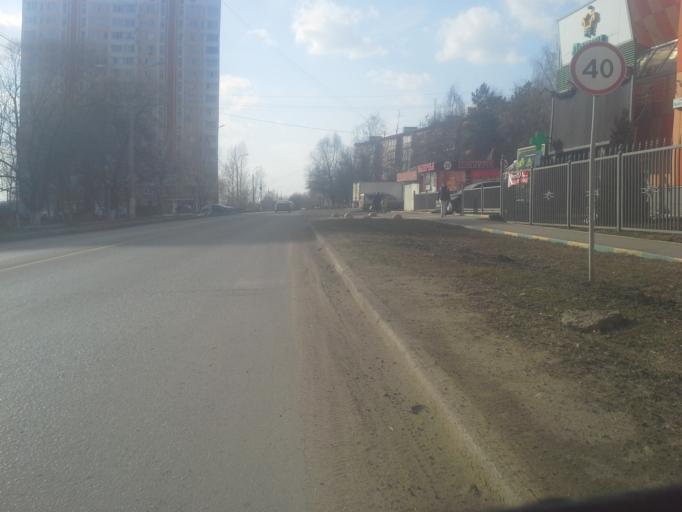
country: RU
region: Moskovskaya
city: Shcherbinka
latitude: 55.4643
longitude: 37.5523
